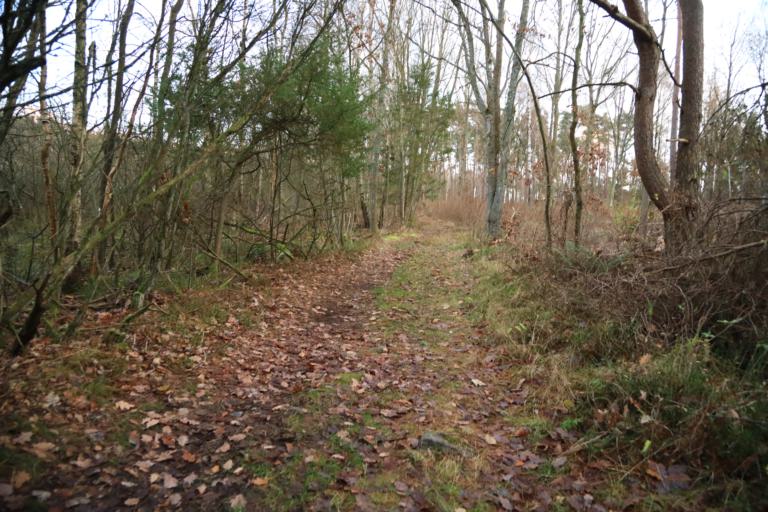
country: SE
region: Halland
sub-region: Varbergs Kommun
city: Varberg
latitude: 57.1464
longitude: 12.2206
